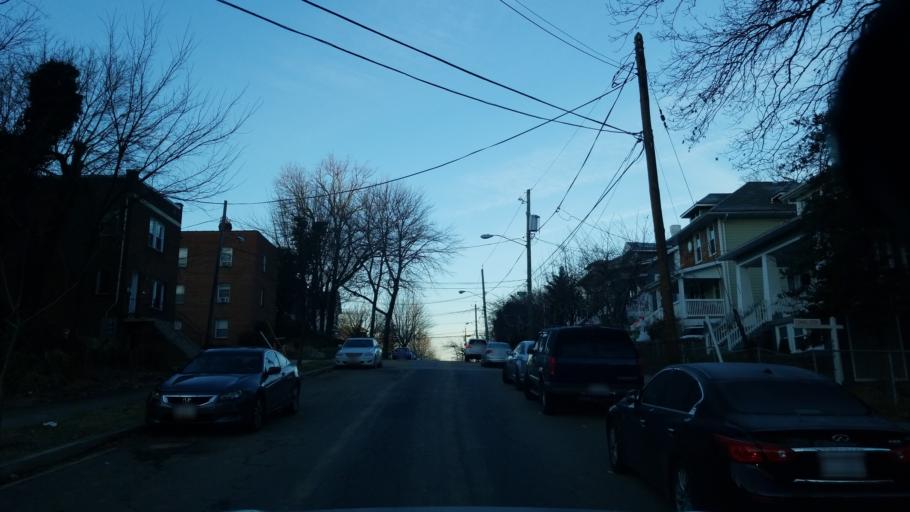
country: US
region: Maryland
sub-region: Prince George's County
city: Silver Hill
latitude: 38.8708
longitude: -76.9695
